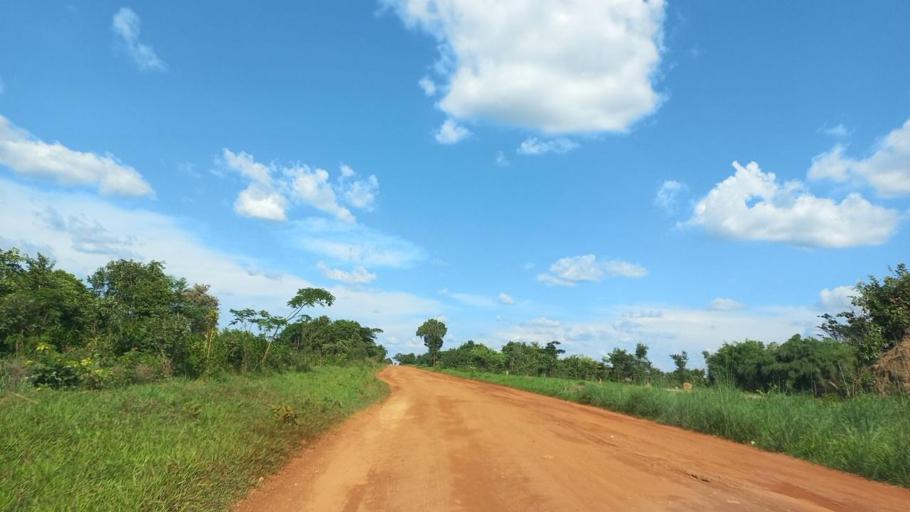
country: ZM
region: Copperbelt
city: Kitwe
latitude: -12.8689
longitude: 28.3631
